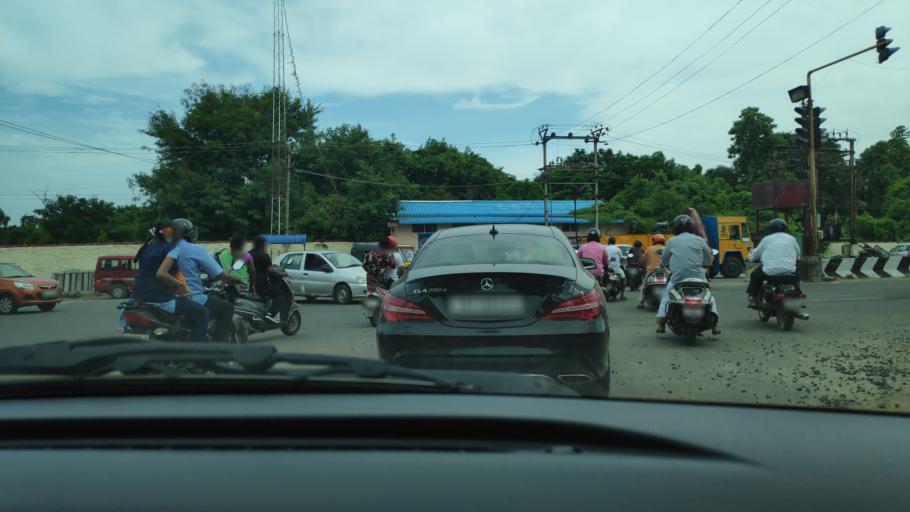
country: IN
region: Tamil Nadu
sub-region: Kancheepuram
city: Vengavasal
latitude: 12.9232
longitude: 80.1257
